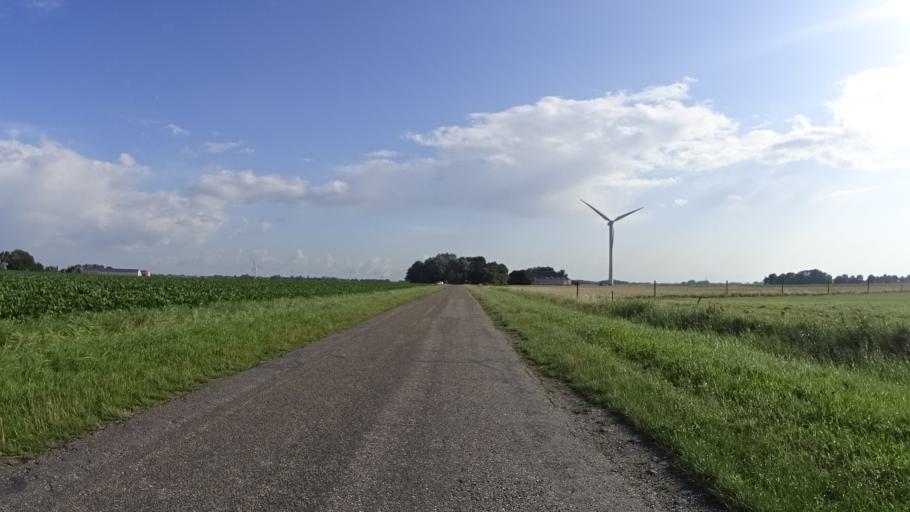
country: NL
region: Friesland
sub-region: Gemeente Harlingen
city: Harlingen
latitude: 53.1203
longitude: 5.4299
